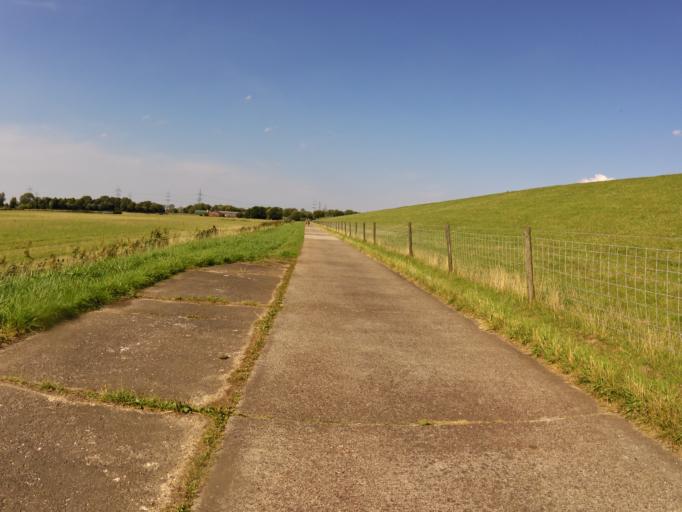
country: DE
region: Lower Saxony
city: Nordenham
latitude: 53.4195
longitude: 8.4725
